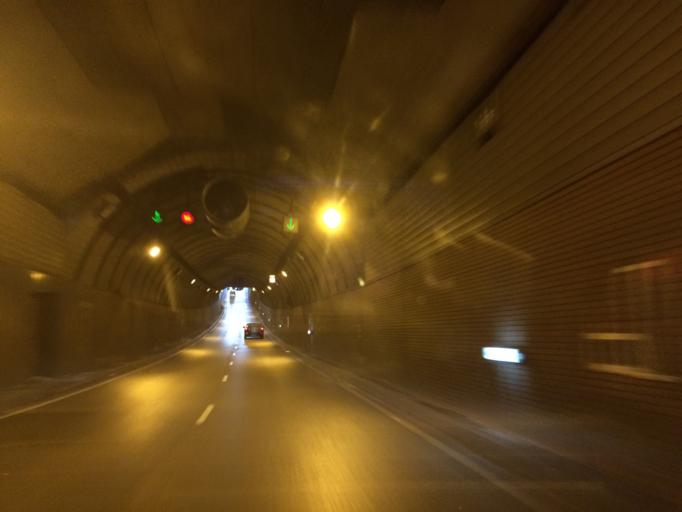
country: ES
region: Madrid
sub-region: Provincia de Madrid
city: Chamberi
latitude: 40.4470
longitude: -3.7054
